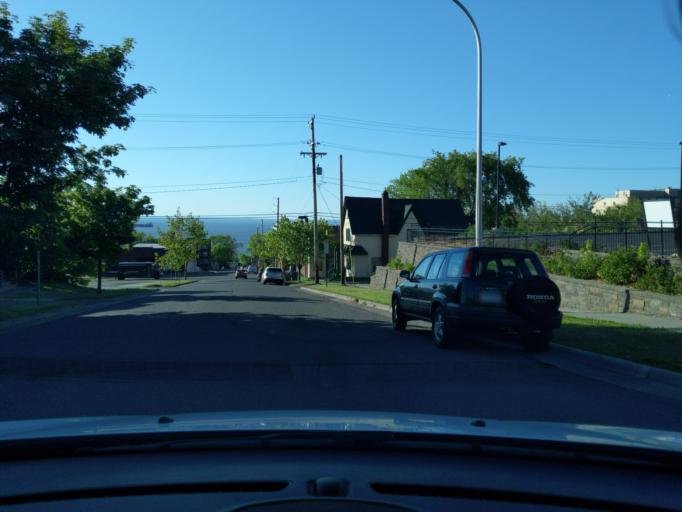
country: US
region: Minnesota
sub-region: Saint Louis County
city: Duluth
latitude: 46.7963
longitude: -92.0937
